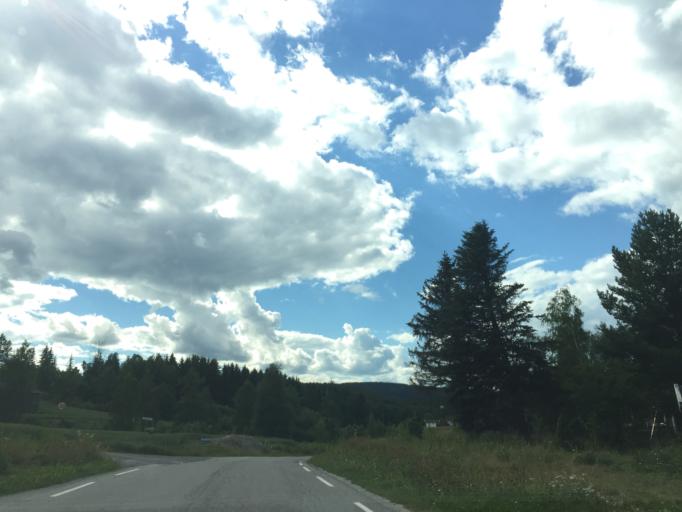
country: NO
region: Hedmark
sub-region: Kongsvinger
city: Spetalen
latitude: 60.1929
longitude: 11.8384
